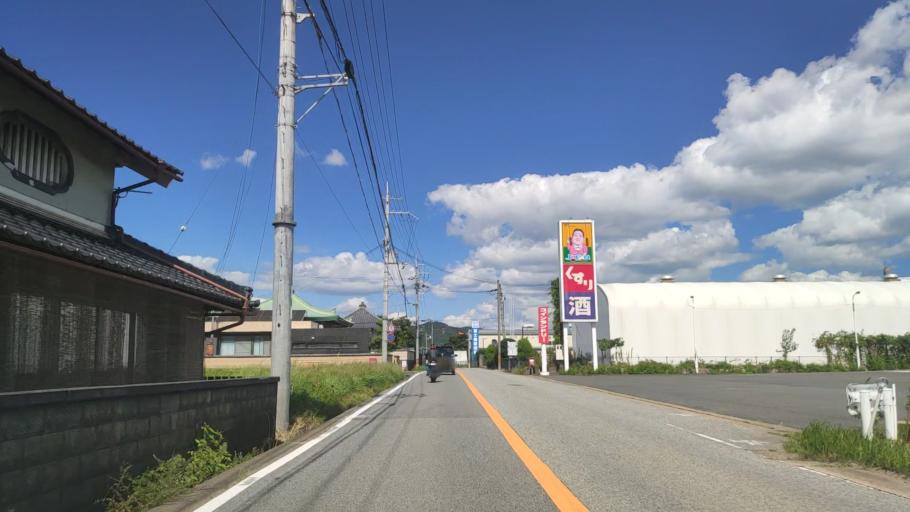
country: JP
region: Kyoto
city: Fukuchiyama
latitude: 35.2226
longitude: 135.1301
